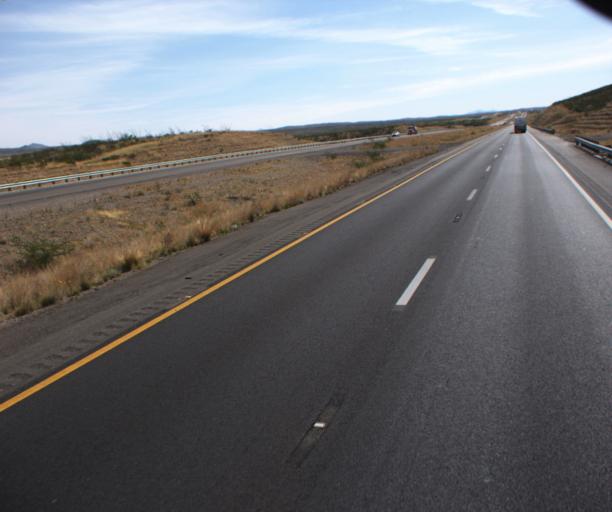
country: US
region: Arizona
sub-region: Cochise County
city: Mescal
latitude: 31.9869
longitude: -110.5785
